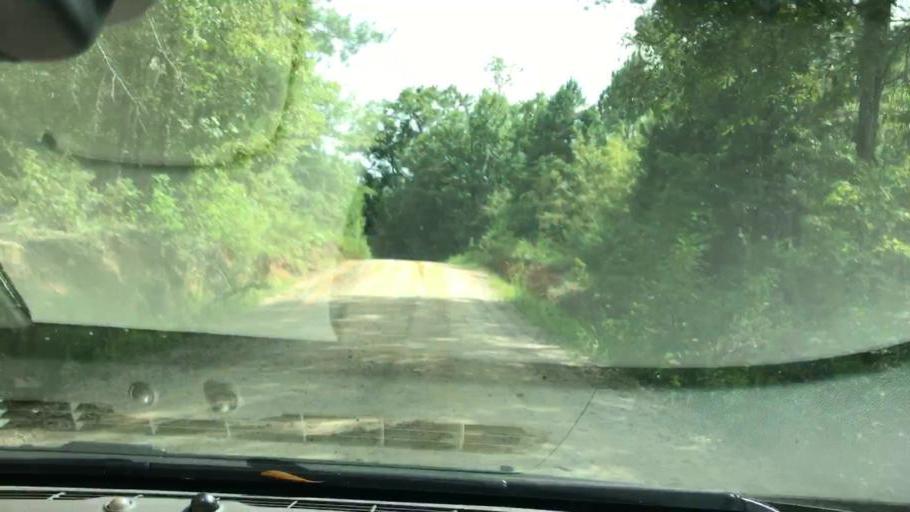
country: US
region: Georgia
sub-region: Clay County
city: Fort Gaines
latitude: 31.7239
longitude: -85.0752
